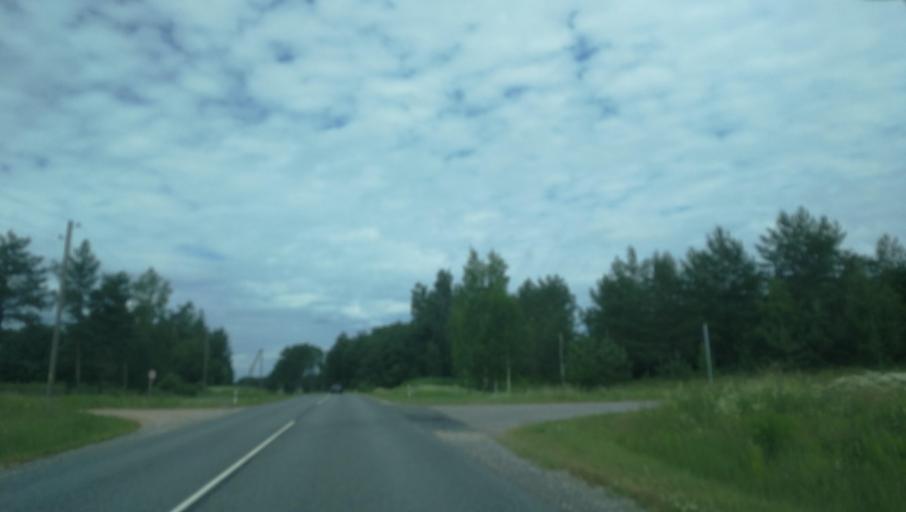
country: LV
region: Naukseni
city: Naukseni
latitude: 57.7470
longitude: 25.4321
